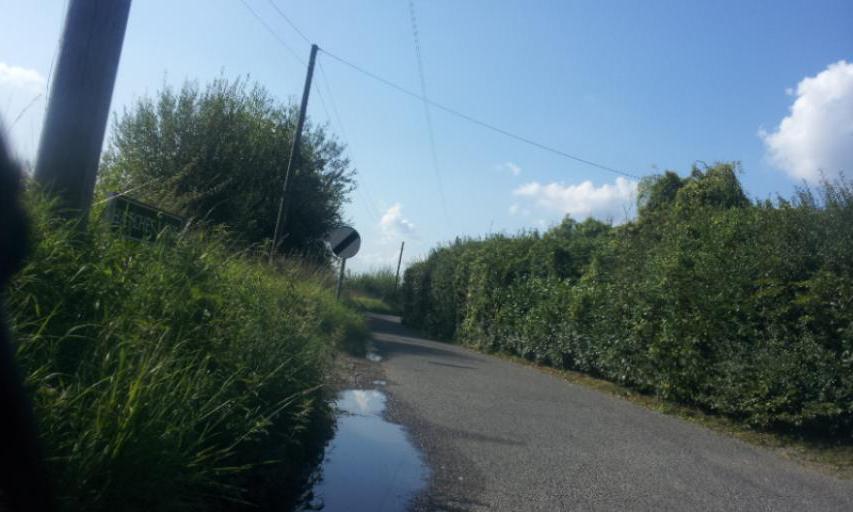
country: GB
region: England
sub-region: Kent
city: East Peckham
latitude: 51.2140
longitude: 0.3777
